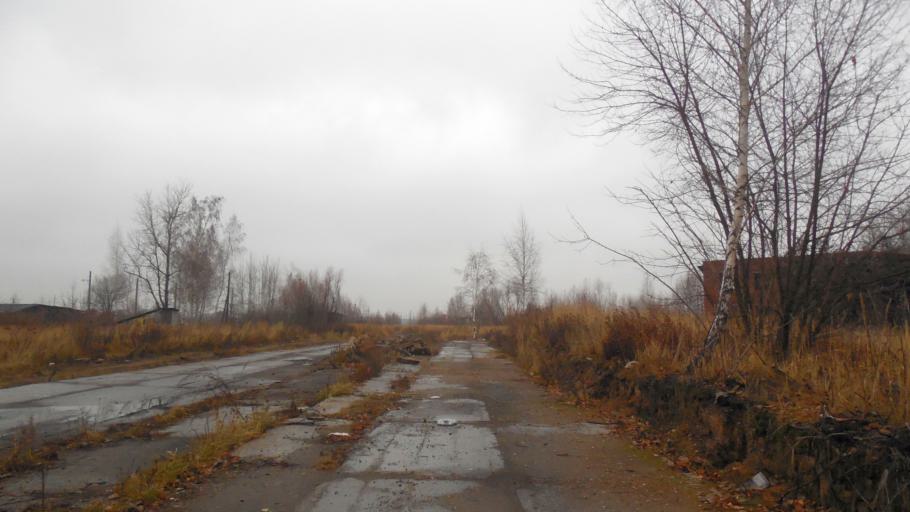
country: RU
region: Moskovskaya
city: Barybino
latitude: 55.2637
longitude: 37.9031
